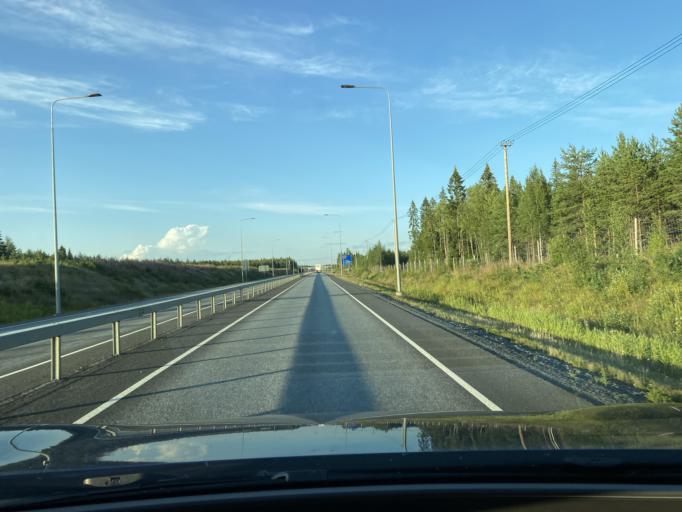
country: FI
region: Southern Ostrobothnia
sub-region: Seinaejoki
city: Seinaejoki
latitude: 62.7171
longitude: 22.8592
